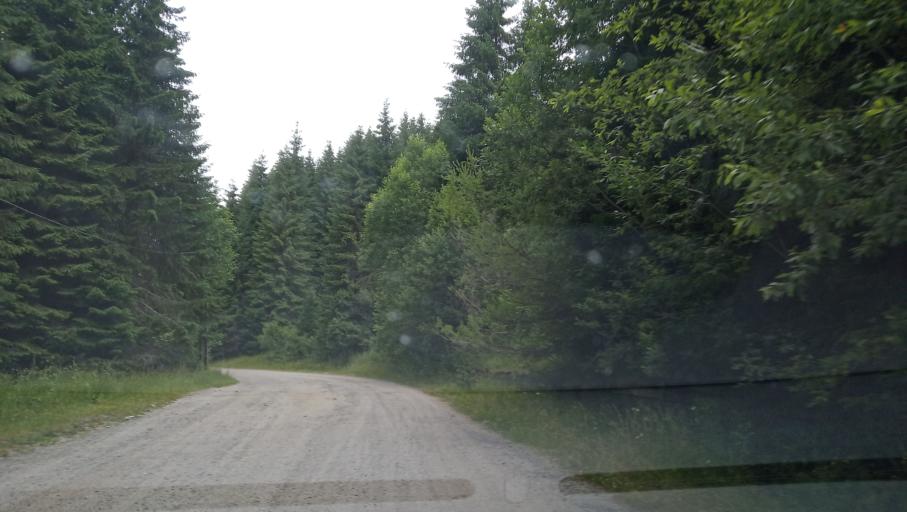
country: RO
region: Valcea
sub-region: Comuna Voineasa
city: Voineasa
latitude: 45.4252
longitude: 23.7628
